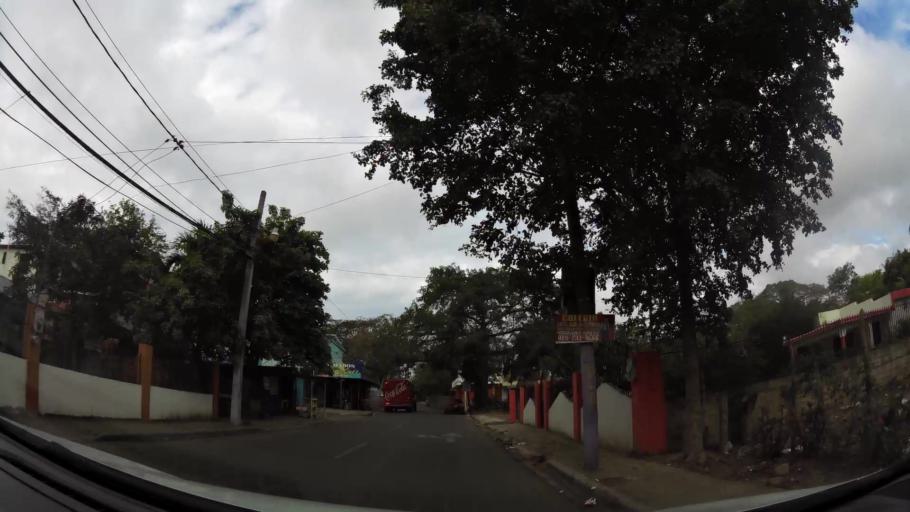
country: DO
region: Santiago
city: Santiago de los Caballeros
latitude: 19.4264
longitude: -70.6586
